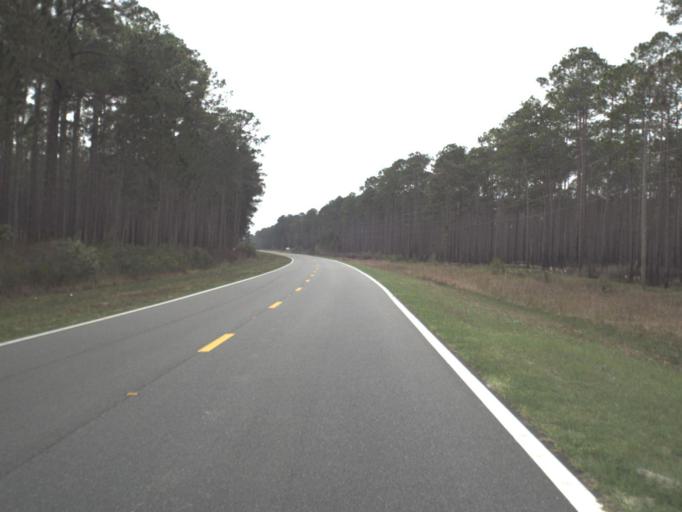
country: US
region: Florida
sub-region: Liberty County
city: Bristol
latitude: 30.1865
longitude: -84.9321
